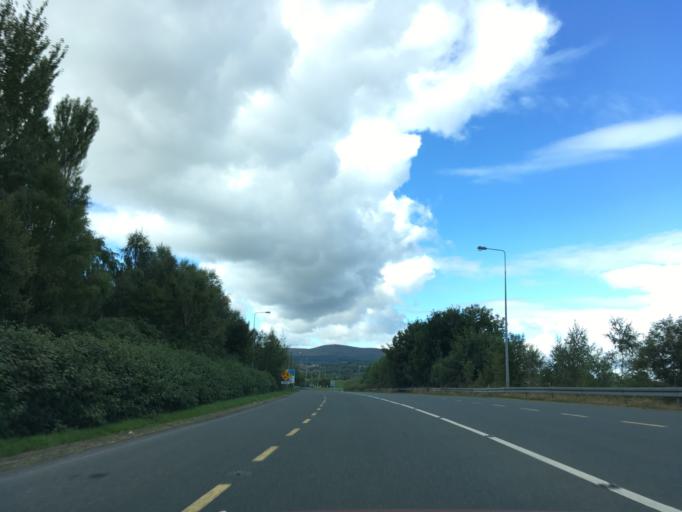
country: IE
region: Munster
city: Cahir
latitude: 52.4000
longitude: -7.9067
